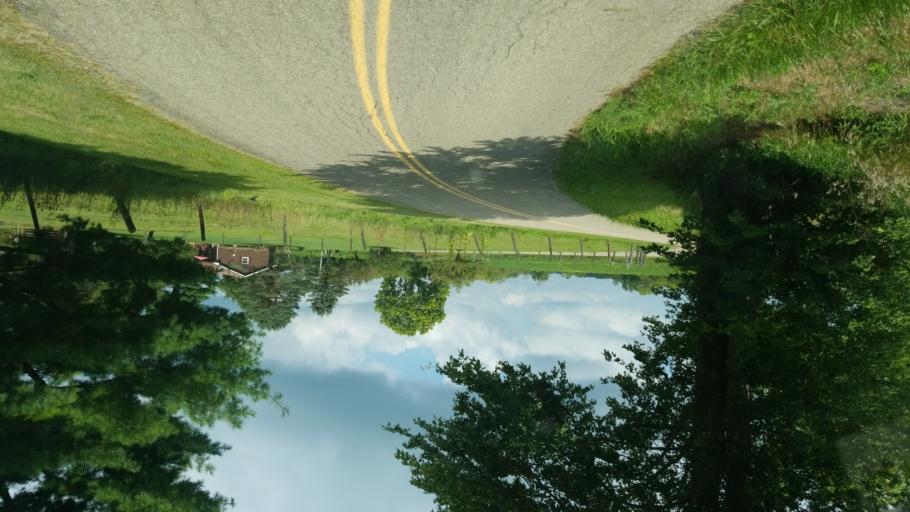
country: US
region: Ohio
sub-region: Licking County
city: Utica
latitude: 40.2695
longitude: -82.4898
